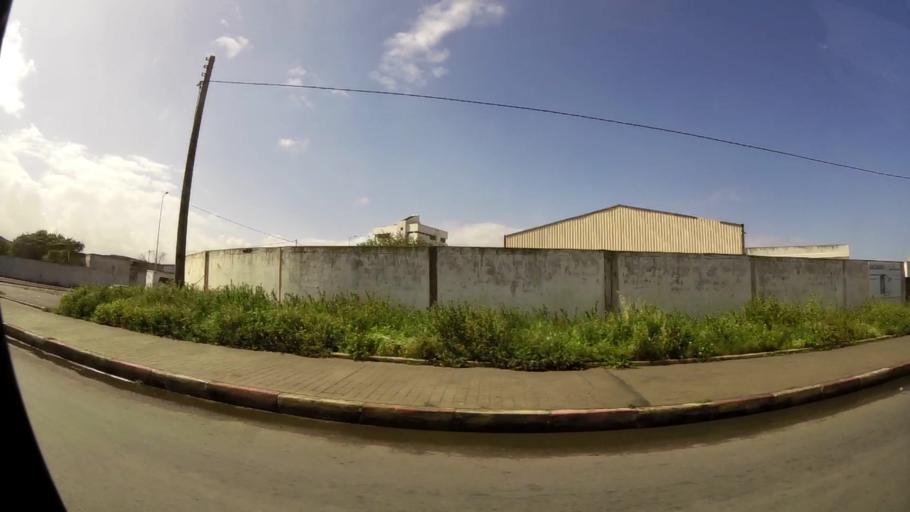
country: MA
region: Grand Casablanca
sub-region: Mediouna
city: Tit Mellil
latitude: 33.6273
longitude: -7.5150
